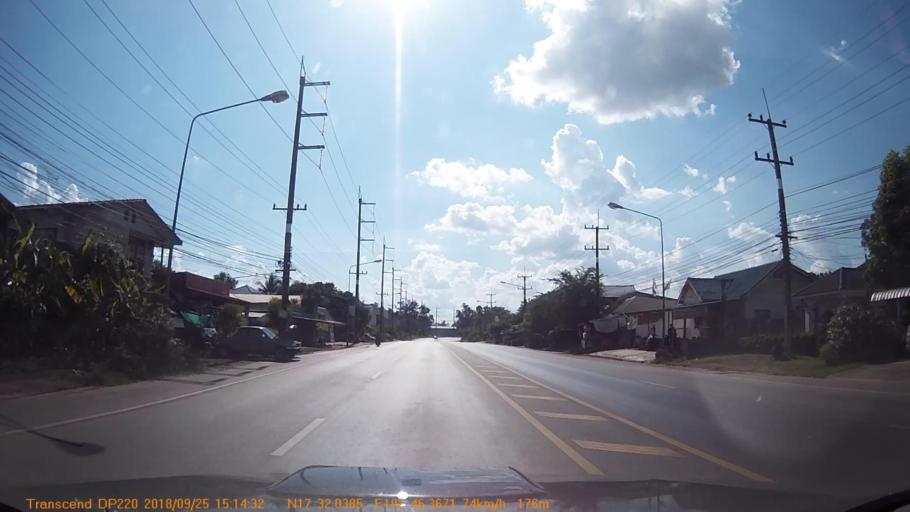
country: TH
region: Changwat Udon Thani
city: Udon Thani
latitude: 17.5339
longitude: 102.7723
